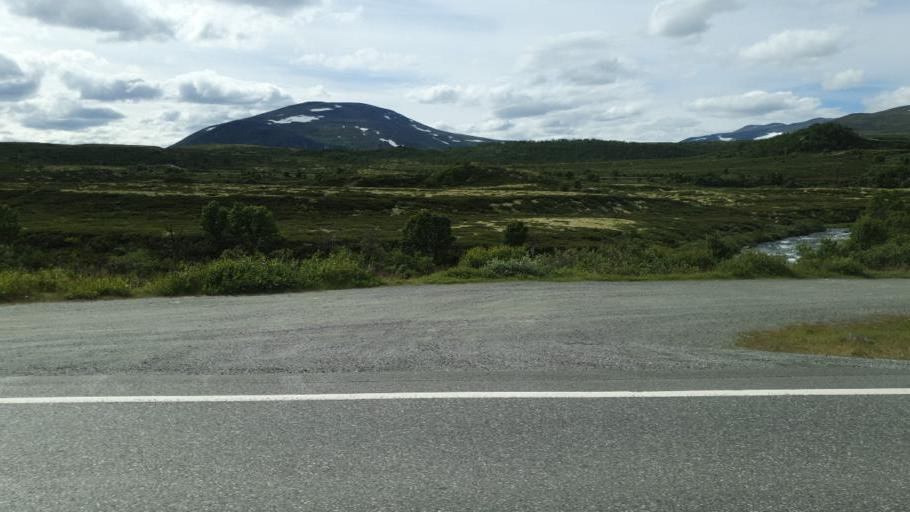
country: NO
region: Sor-Trondelag
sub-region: Oppdal
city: Oppdal
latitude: 62.2805
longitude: 9.5994
